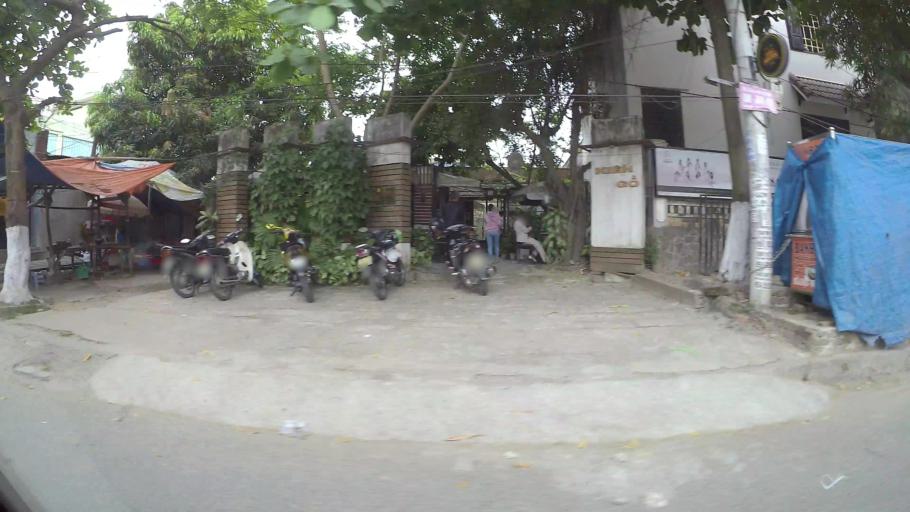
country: VN
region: Da Nang
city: Lien Chieu
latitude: 16.0720
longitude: 108.1424
